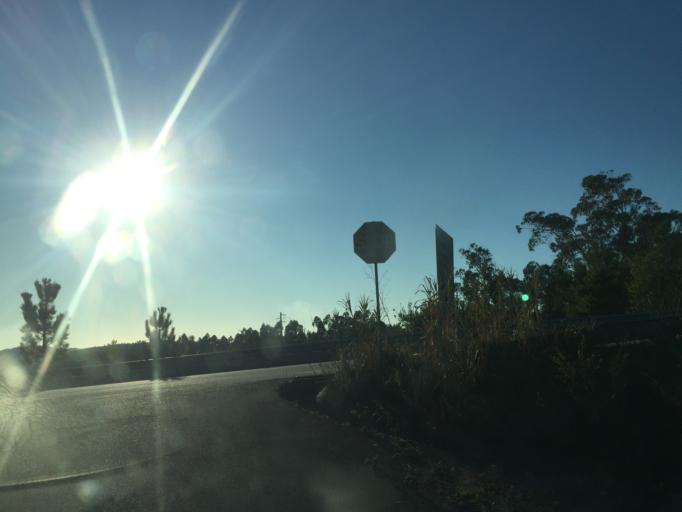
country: PT
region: Coimbra
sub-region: Figueira da Foz
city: Alhadas
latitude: 40.1779
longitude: -8.7989
